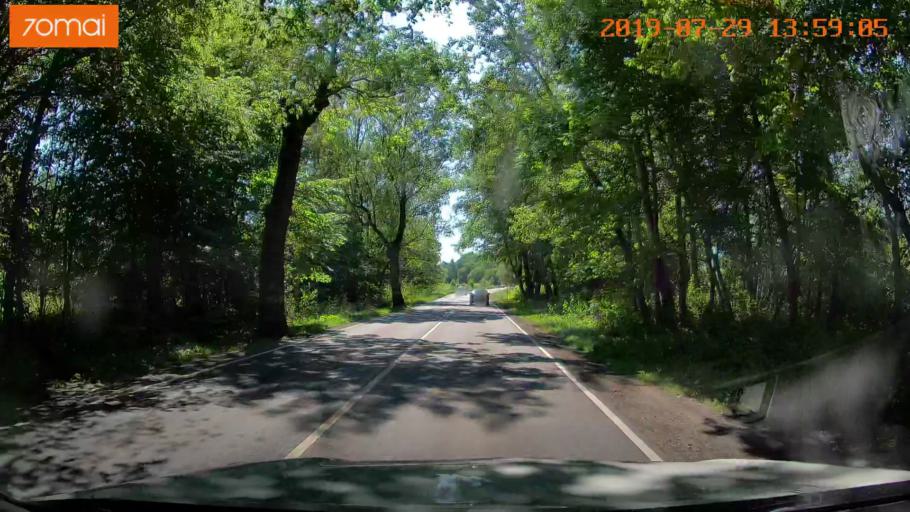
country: RU
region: Kaliningrad
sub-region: Gorod Kaliningrad
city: Baltiysk
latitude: 54.6875
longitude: 19.9342
